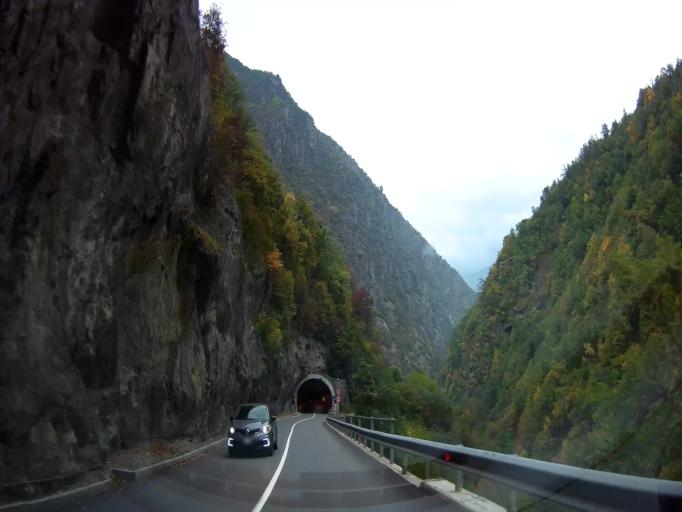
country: IT
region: Trentino-Alto Adige
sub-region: Bolzano
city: Naturno
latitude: 46.6554
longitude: 10.9681
